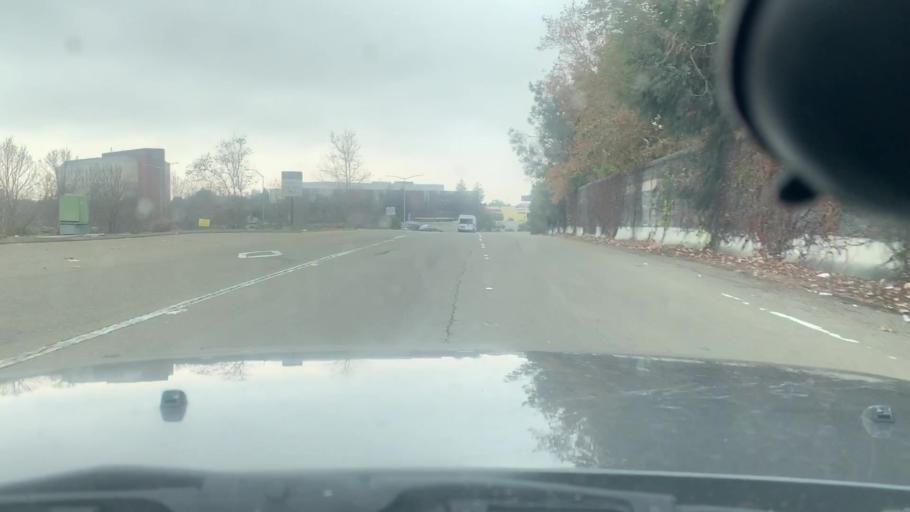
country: US
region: California
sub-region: Alameda County
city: Fremont
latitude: 37.5239
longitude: -121.9876
